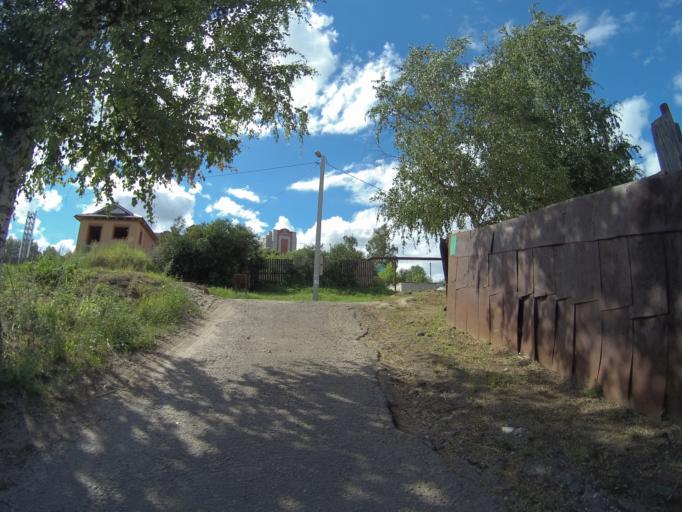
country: RU
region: Vladimir
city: Vladimir
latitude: 56.1095
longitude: 40.3779
